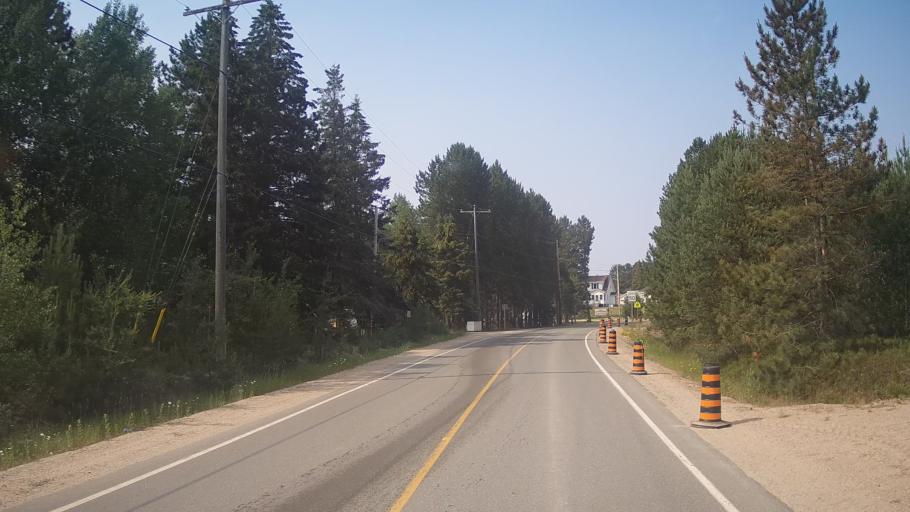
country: CA
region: Ontario
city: Timmins
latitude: 47.6767
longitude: -81.7184
